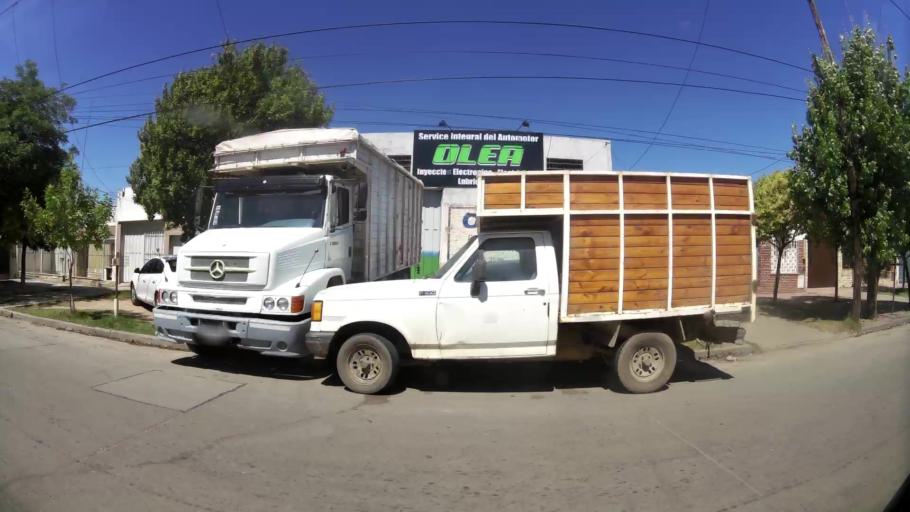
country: AR
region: Cordoba
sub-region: Departamento de Capital
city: Cordoba
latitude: -31.3697
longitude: -64.1478
